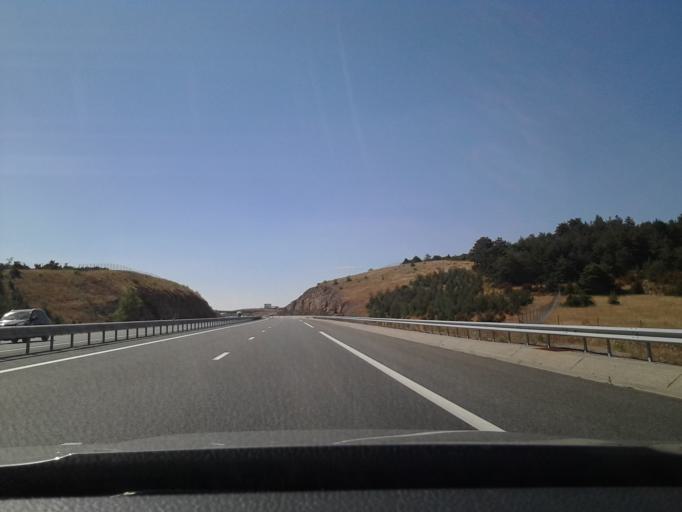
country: FR
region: Midi-Pyrenees
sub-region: Departement de l'Aveyron
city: Creissels
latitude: 44.0393
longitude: 3.0594
